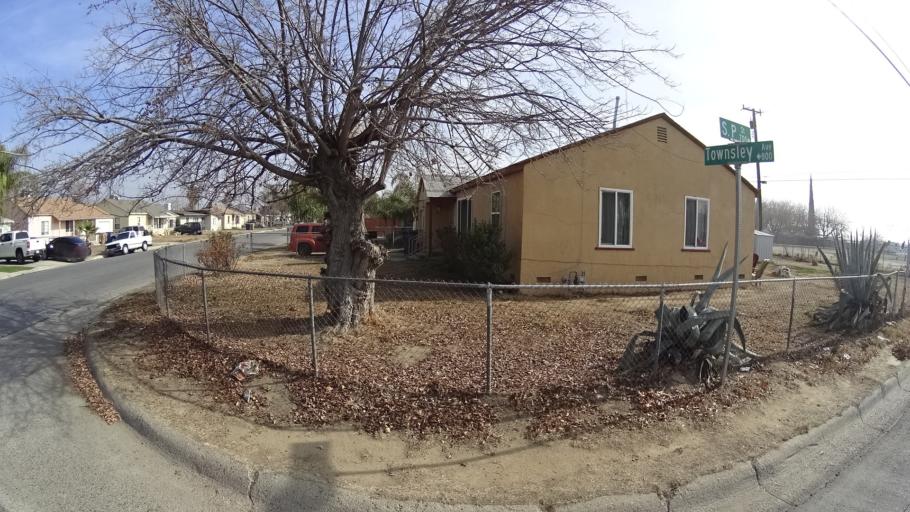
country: US
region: California
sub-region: Kern County
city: Bakersfield
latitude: 35.3488
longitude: -119.0118
